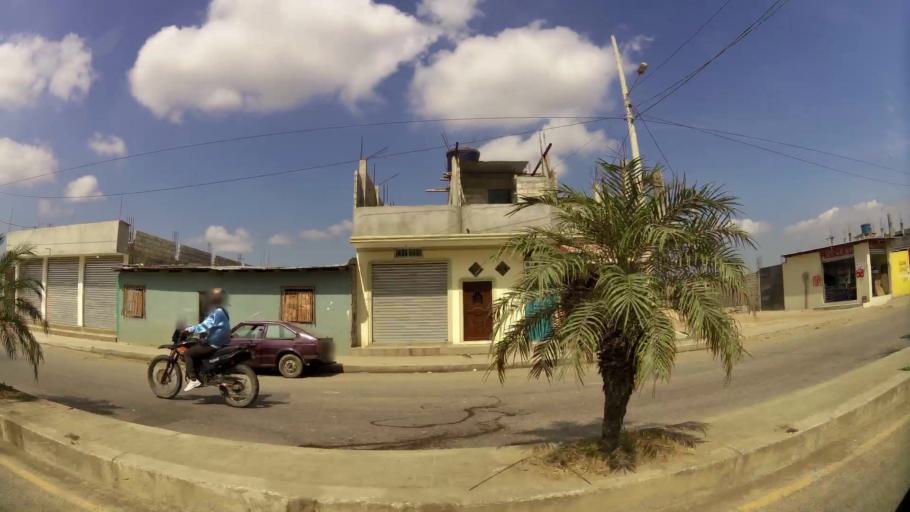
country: EC
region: Guayas
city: Eloy Alfaro
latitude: -2.1680
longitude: -79.8303
